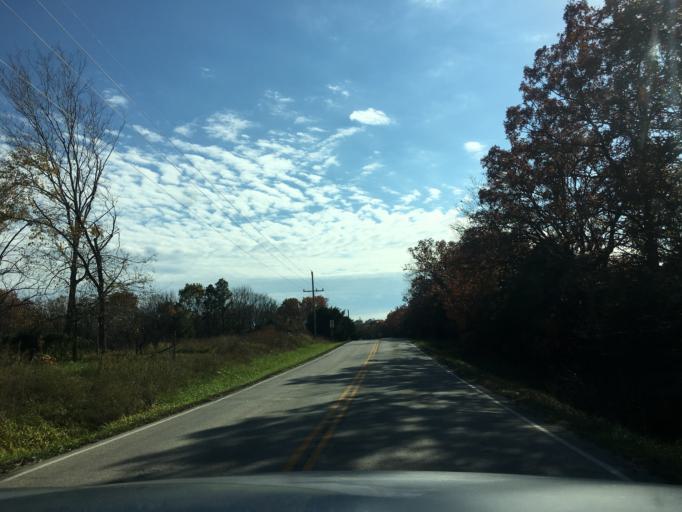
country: US
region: Missouri
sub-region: Maries County
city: Belle
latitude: 38.3353
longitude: -91.7626
